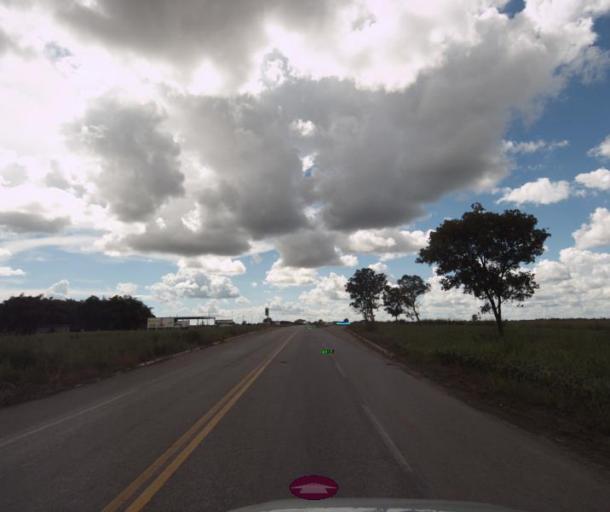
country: BR
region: Goias
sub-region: Porangatu
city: Porangatu
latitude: -13.5297
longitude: -49.1121
